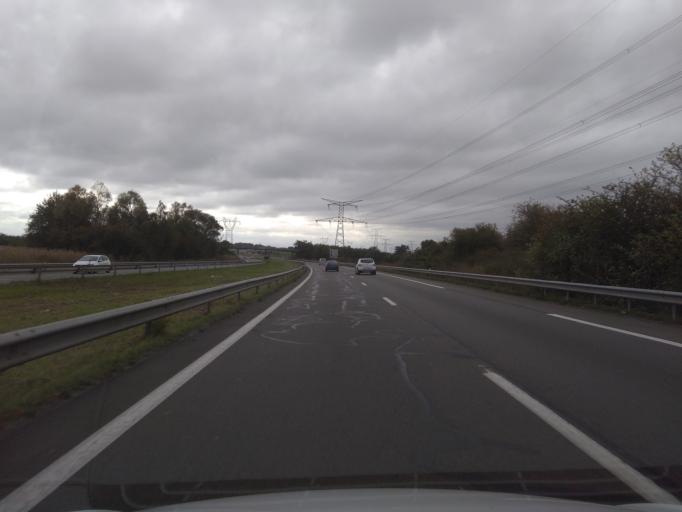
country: FR
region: Nord-Pas-de-Calais
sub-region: Departement du Nord
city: Orchies
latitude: 50.4918
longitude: 3.2123
